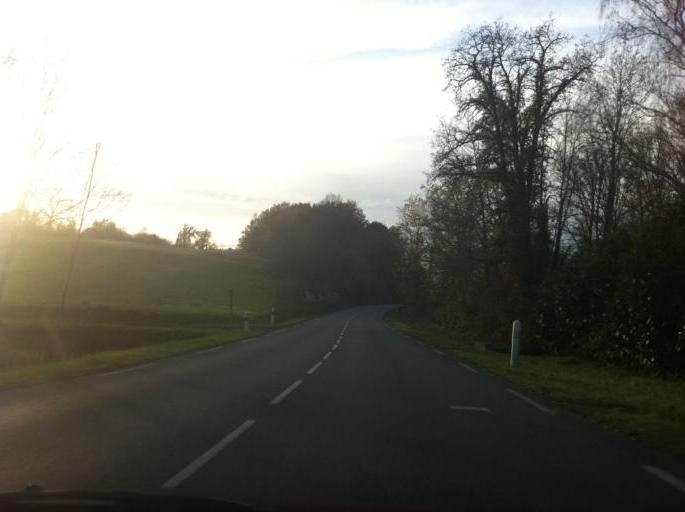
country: FR
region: Aquitaine
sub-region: Departement de la Dordogne
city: Tocane-Saint-Apre
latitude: 45.2584
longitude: 0.5091
